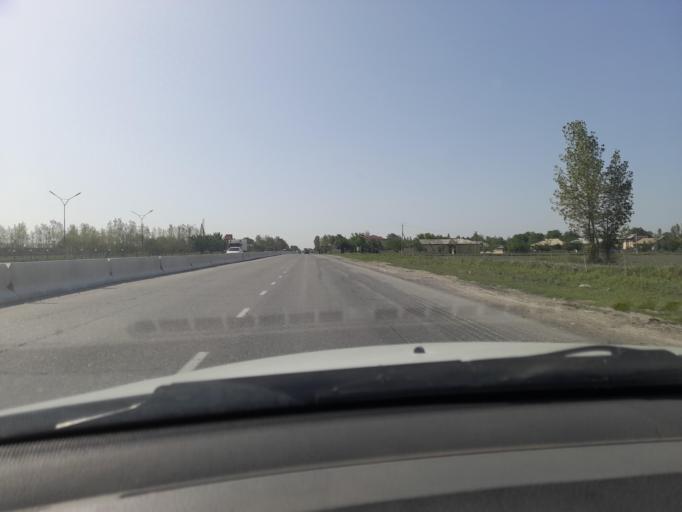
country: UZ
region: Samarqand
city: Chelak
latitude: 39.8369
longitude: 66.8253
